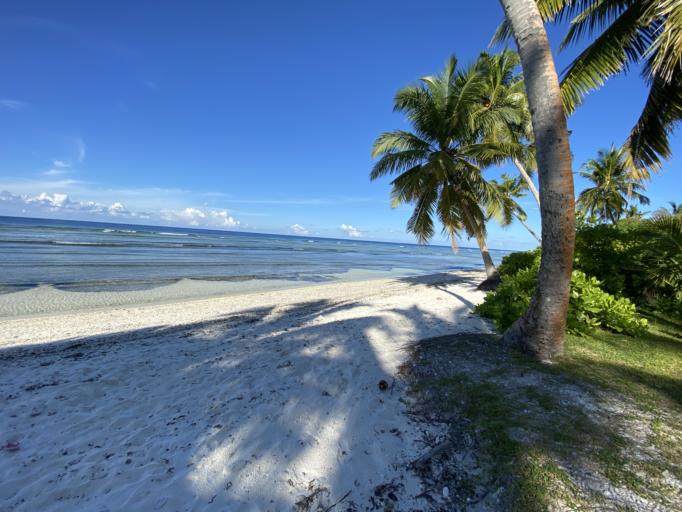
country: MV
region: Seenu
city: Meedhoo
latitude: -0.5802
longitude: 73.2283
